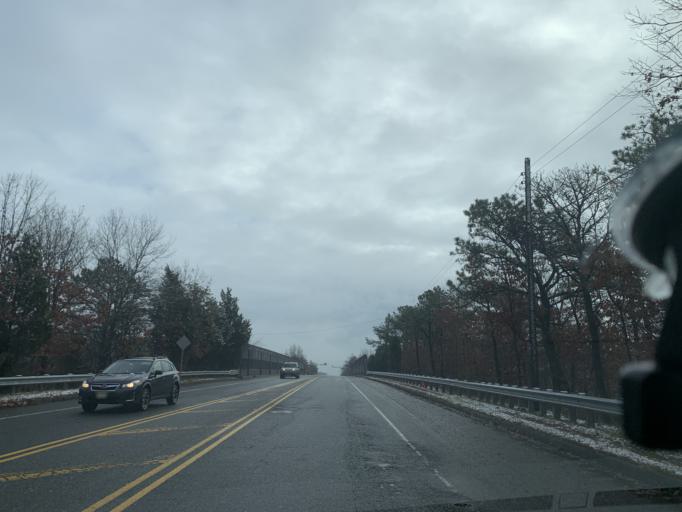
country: US
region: New Jersey
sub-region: Atlantic County
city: Pomona
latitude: 39.4341
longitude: -74.5884
